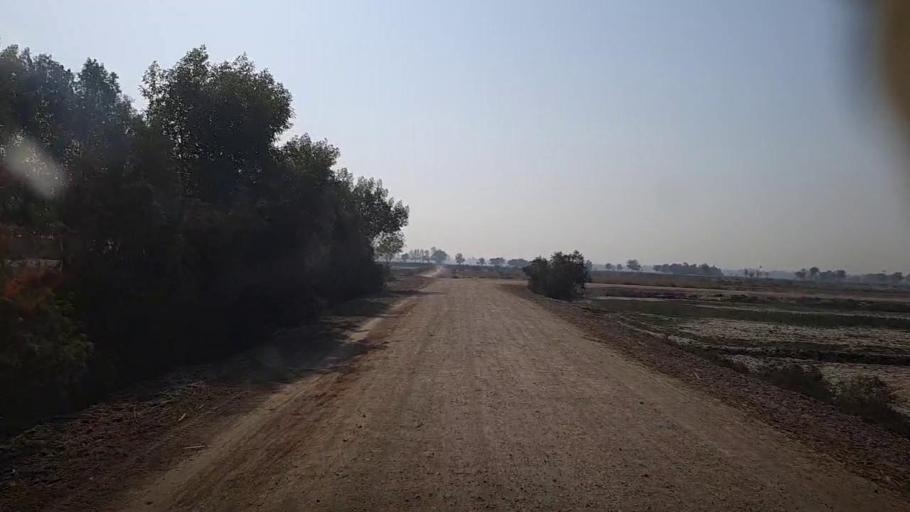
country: PK
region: Sindh
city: Karaundi
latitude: 26.8480
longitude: 68.3993
